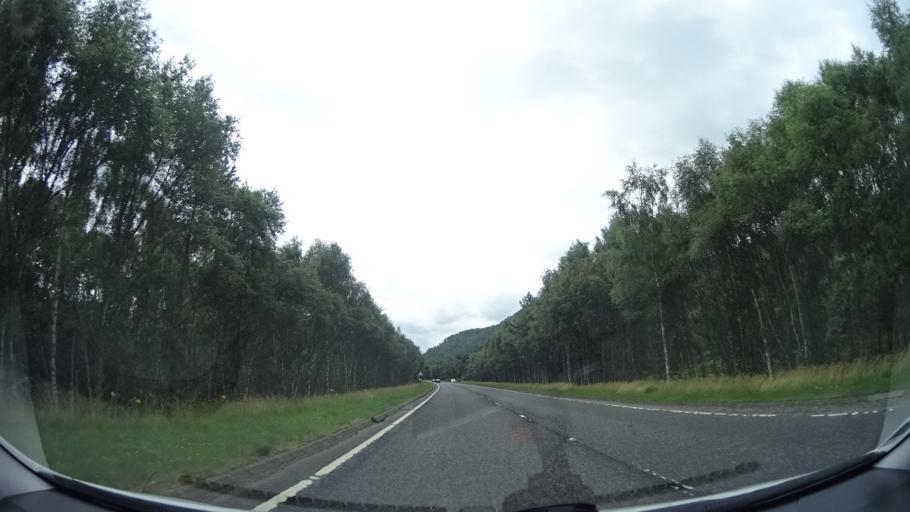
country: GB
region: Scotland
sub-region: Highland
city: Aviemore
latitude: 57.1923
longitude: -3.8370
